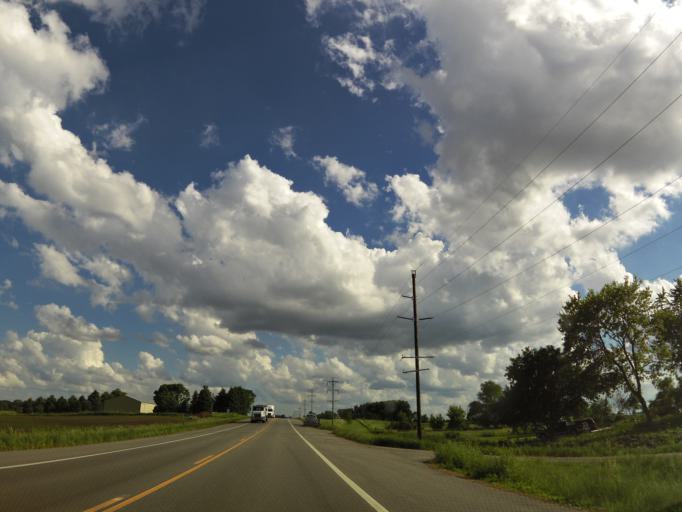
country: US
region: Minnesota
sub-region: Carver County
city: Waconia
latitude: 44.8986
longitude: -93.8186
